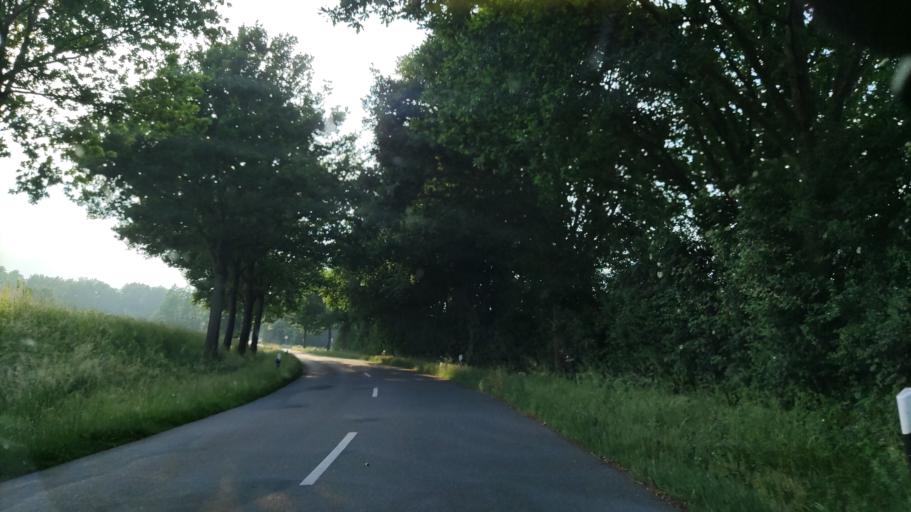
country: DE
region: Lower Saxony
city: Hanstedt Eins
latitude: 53.0315
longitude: 10.3536
